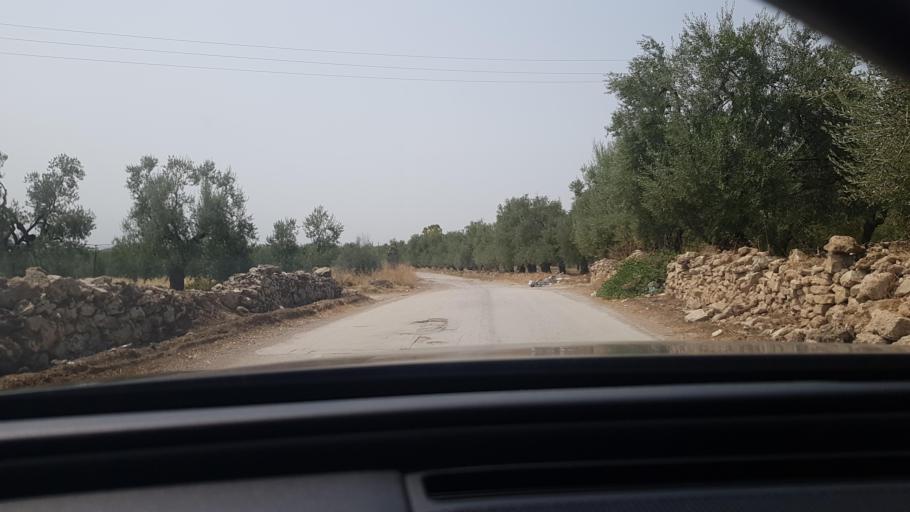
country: IT
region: Apulia
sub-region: Provincia di Barletta - Andria - Trani
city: Andria
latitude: 41.2193
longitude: 16.2625
